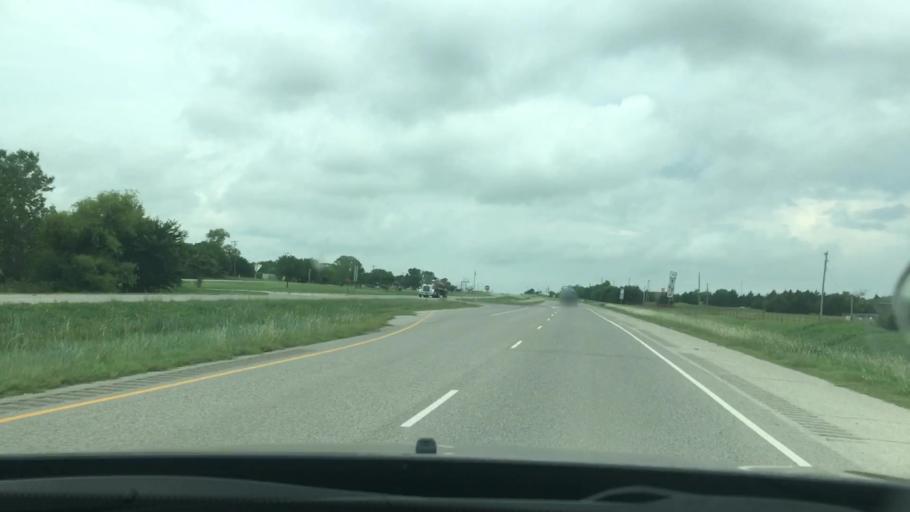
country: US
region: Oklahoma
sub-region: Carter County
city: Wilson
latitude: 34.1735
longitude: -97.4296
